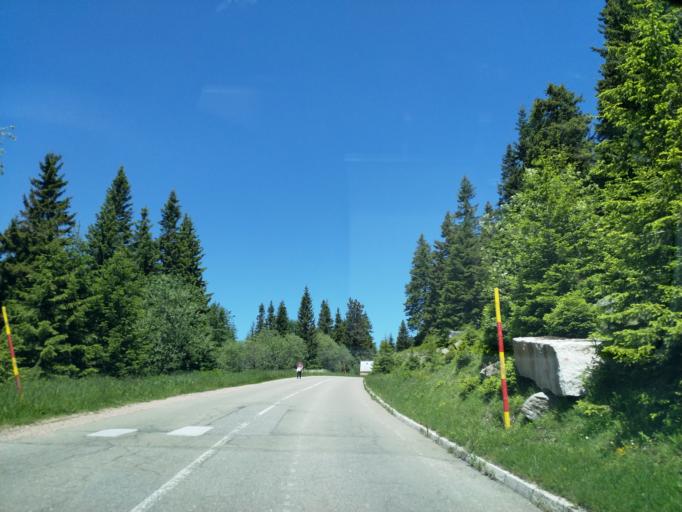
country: XK
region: Mitrovica
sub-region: Komuna e Leposaviqit
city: Leposaviq
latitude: 43.2993
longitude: 20.8200
